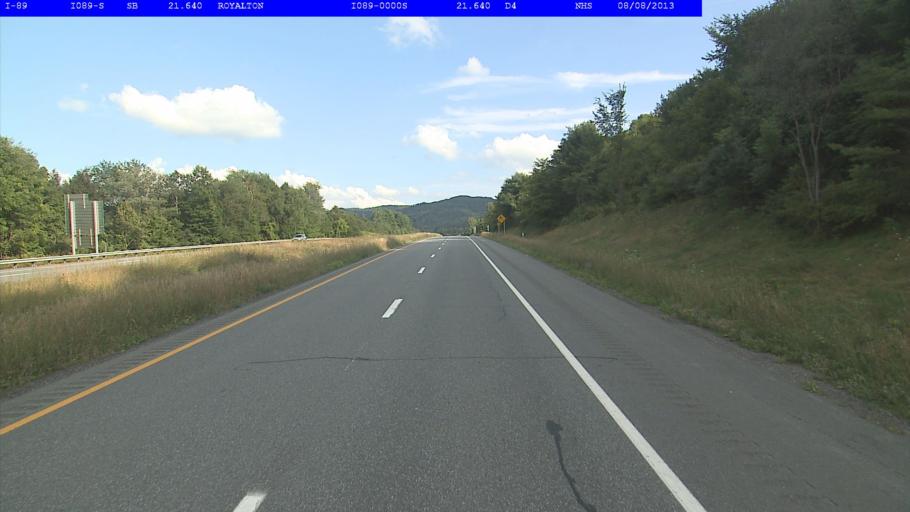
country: US
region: Vermont
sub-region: Orange County
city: Randolph
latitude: 43.8214
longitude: -72.5739
